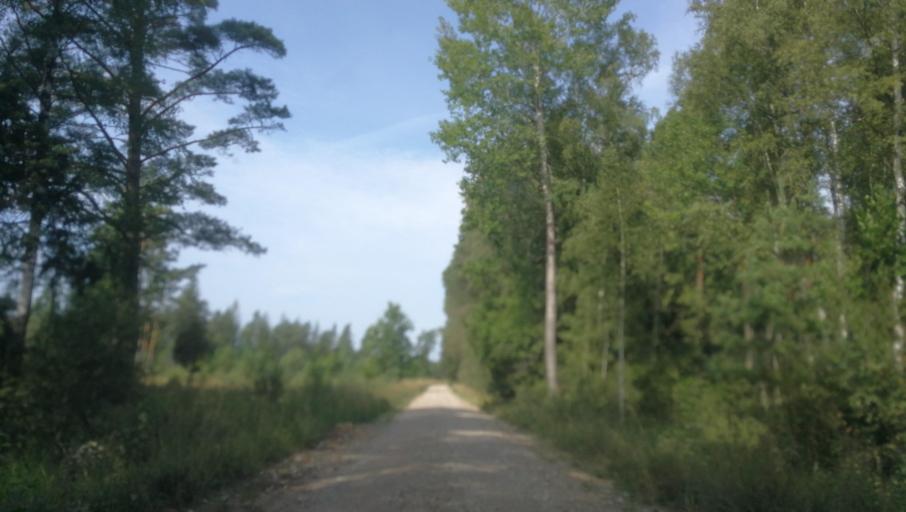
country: LV
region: Pavilostas
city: Pavilosta
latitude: 56.8337
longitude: 21.2830
